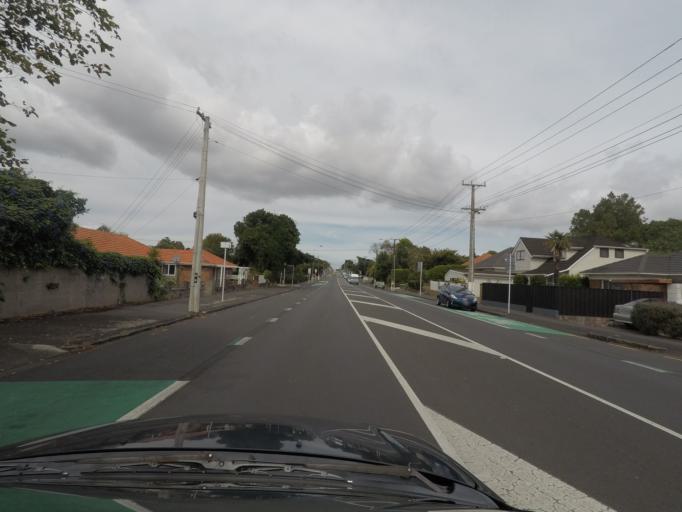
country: NZ
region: Auckland
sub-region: Auckland
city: Auckland
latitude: -36.8805
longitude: 174.7399
